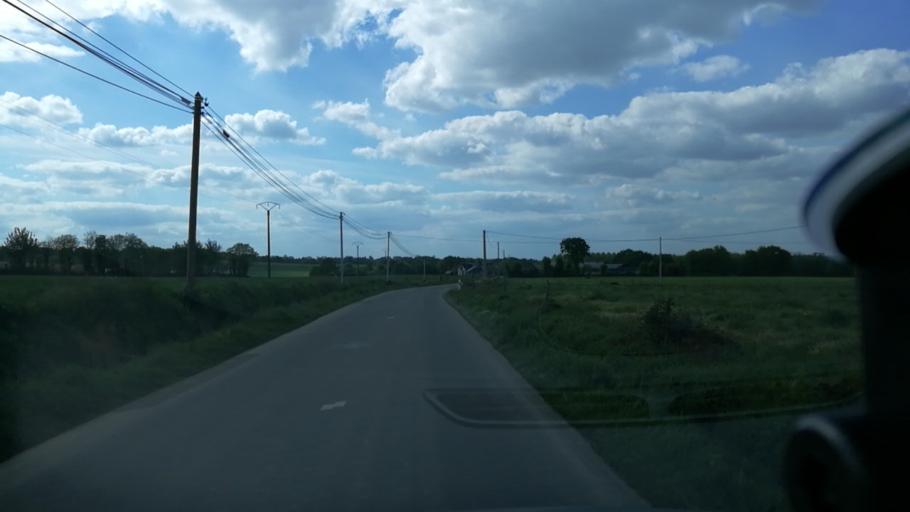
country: FR
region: Brittany
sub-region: Departement d'Ille-et-Vilaine
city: Retiers
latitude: 47.8919
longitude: -1.3407
